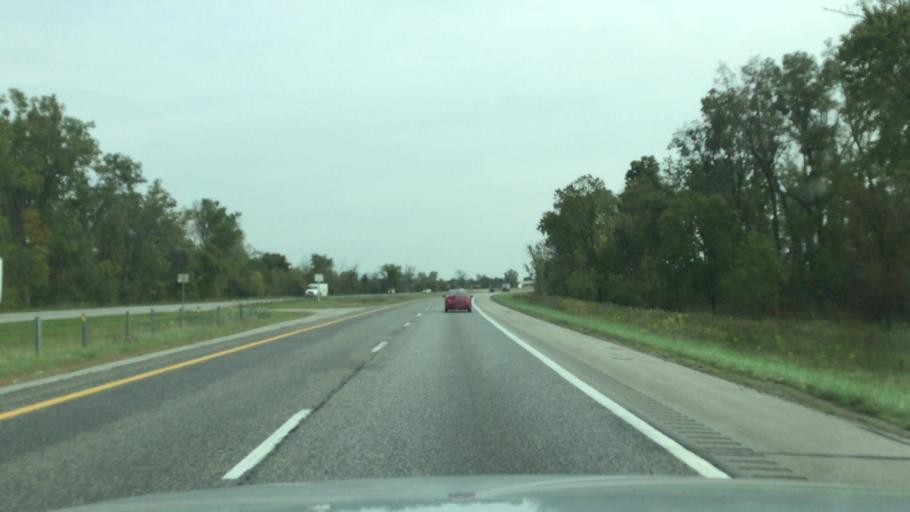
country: US
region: Michigan
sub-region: Shiawassee County
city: Corunna
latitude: 42.8895
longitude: -84.1057
